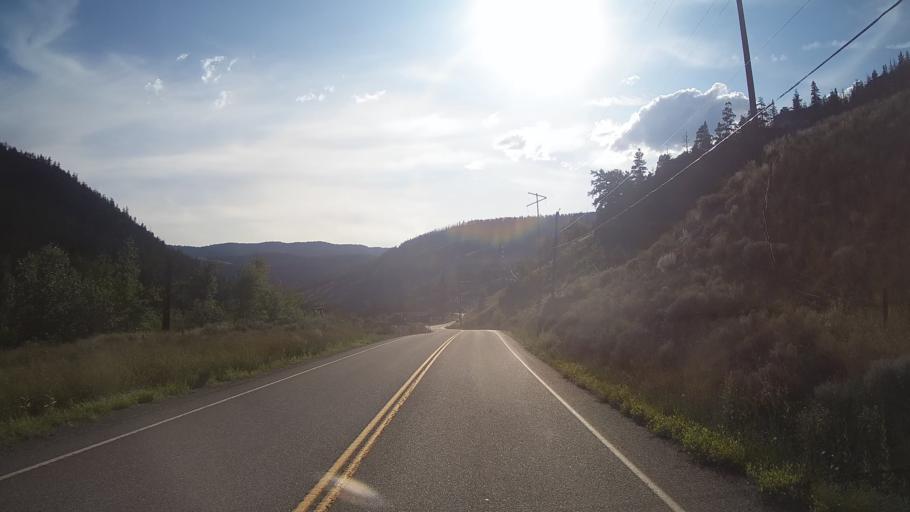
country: CA
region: British Columbia
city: Cache Creek
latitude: 50.8849
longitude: -121.4824
